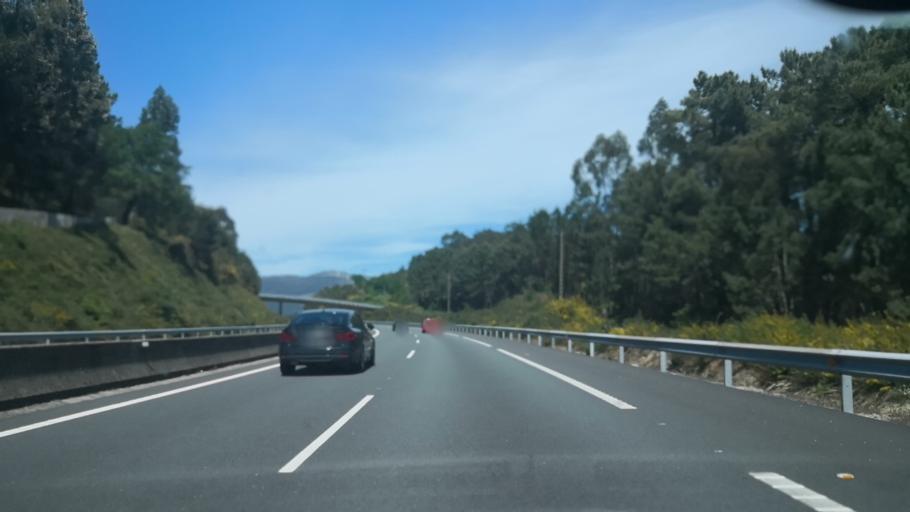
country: ES
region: Galicia
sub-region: Provincia de Pontevedra
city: Portas
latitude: 42.5692
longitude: -8.6704
